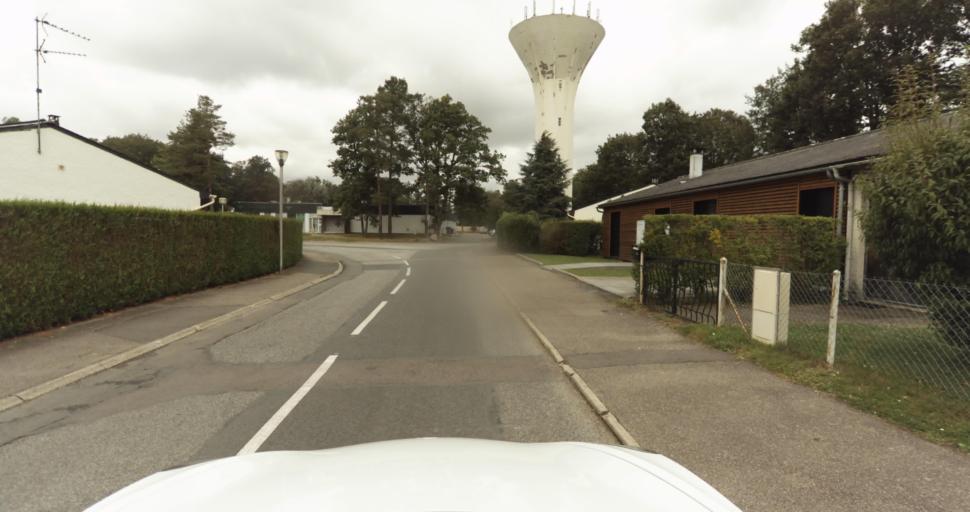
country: FR
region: Haute-Normandie
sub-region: Departement de l'Eure
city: Saint-Sebastien-de-Morsent
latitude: 49.0077
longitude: 1.0932
